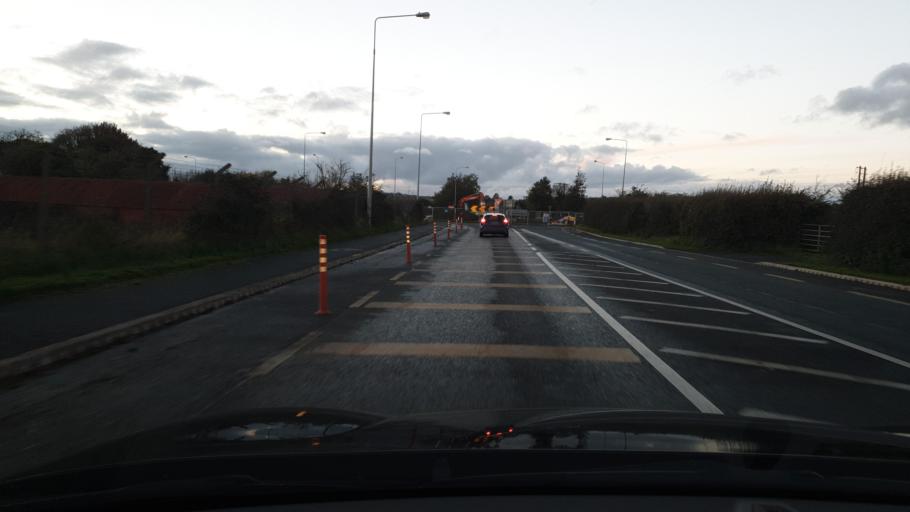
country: IE
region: Leinster
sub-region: Lu
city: Drogheda
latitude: 53.7301
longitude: -6.3728
